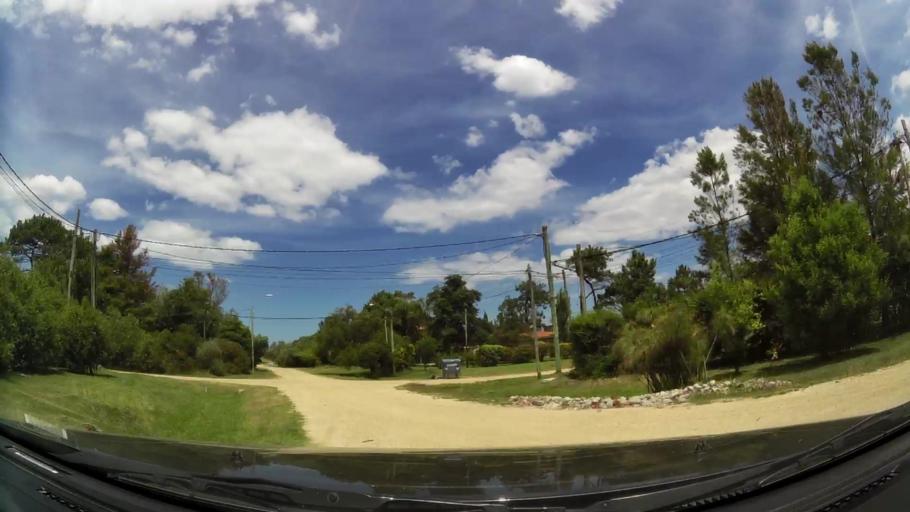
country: UY
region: Canelones
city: Pando
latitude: -34.8047
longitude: -55.8993
